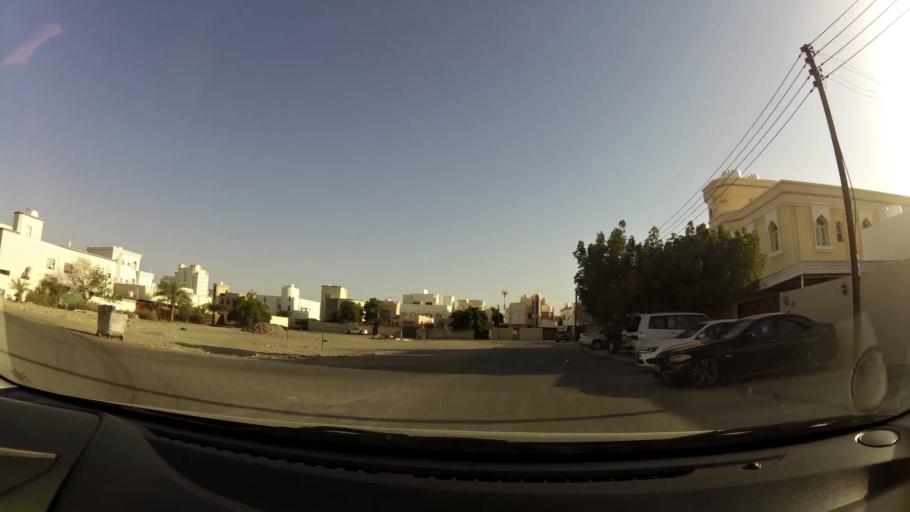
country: OM
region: Muhafazat Masqat
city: As Sib al Jadidah
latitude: 23.6345
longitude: 58.1969
